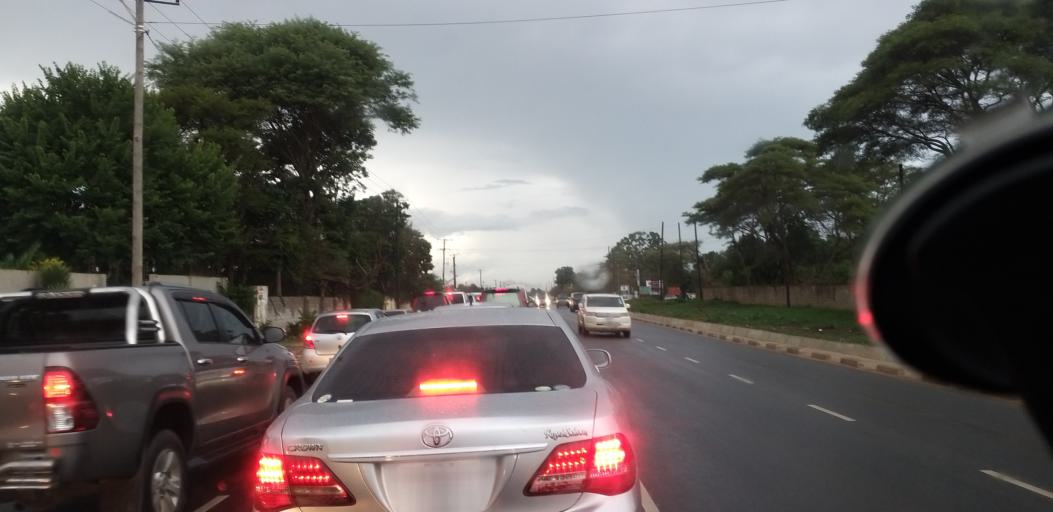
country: ZM
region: Lusaka
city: Lusaka
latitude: -15.4288
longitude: 28.3558
